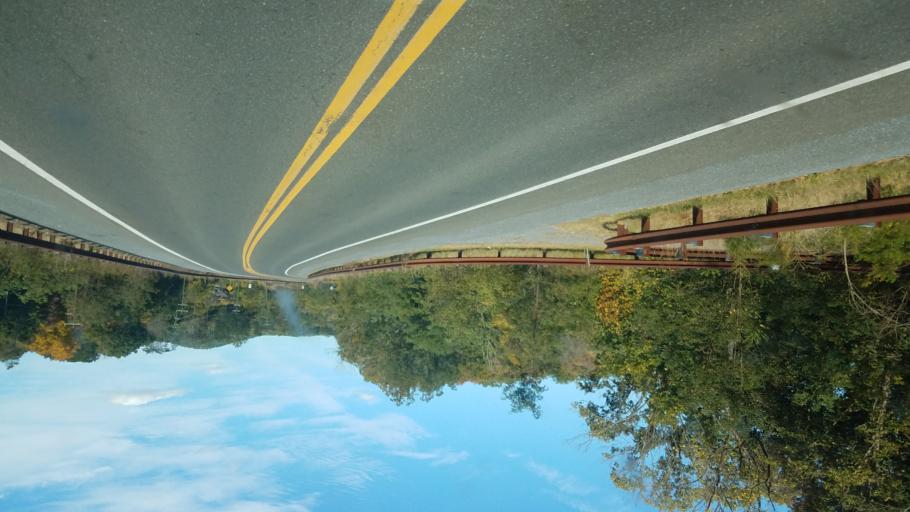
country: US
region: Virginia
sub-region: Shenandoah County
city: Woodstock
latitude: 38.8018
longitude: -78.3543
